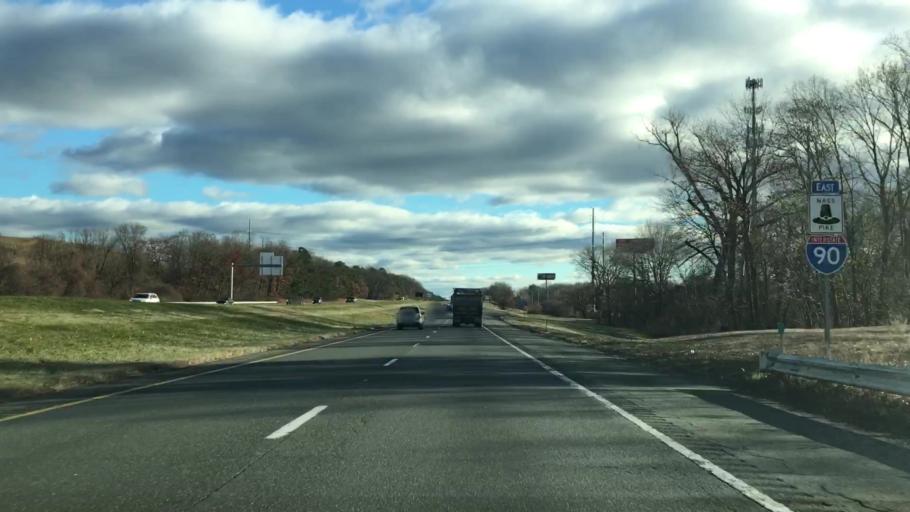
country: US
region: Massachusetts
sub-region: Hampden County
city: Ludlow
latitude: 42.1616
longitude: -72.5331
